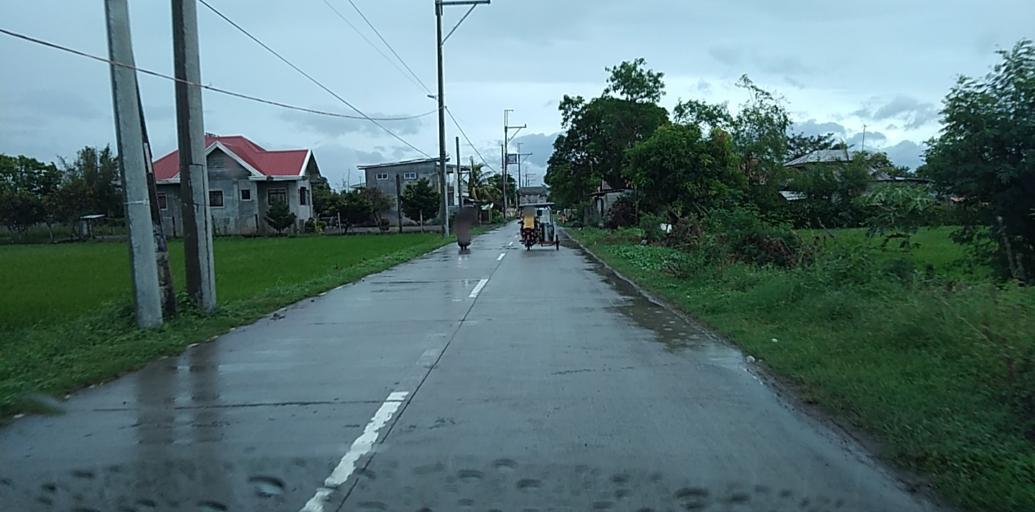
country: PH
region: Central Luzon
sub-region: Province of Pampanga
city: Salapungan
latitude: 15.1347
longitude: 120.9211
